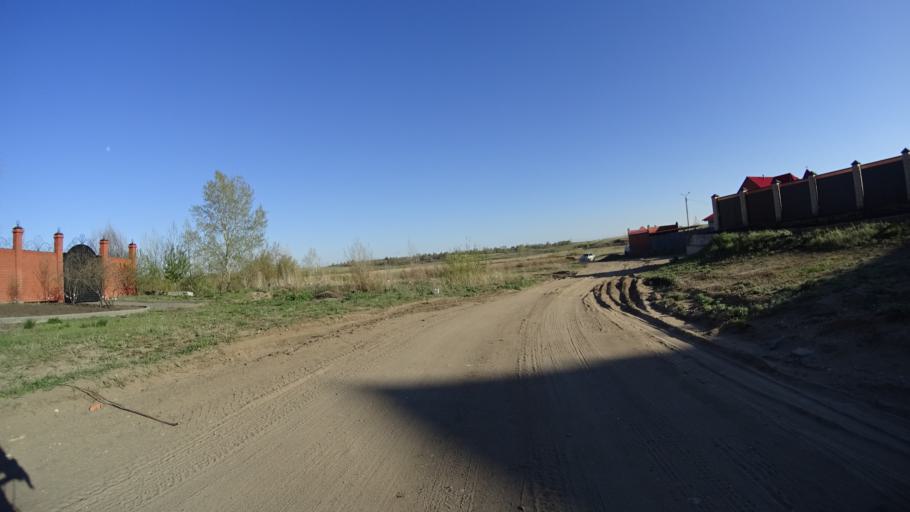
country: RU
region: Chelyabinsk
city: Troitsk
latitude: 54.0693
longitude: 61.5379
